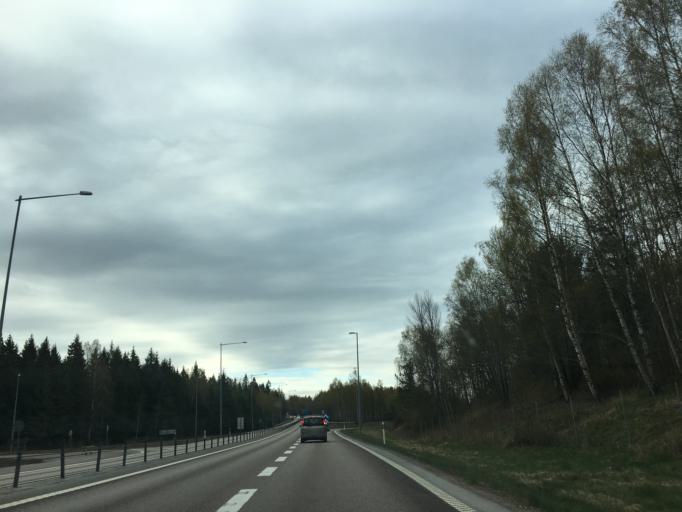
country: SE
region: Vaermland
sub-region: Kristinehamns Kommun
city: Kristinehamn
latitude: 59.3323
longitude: 14.0966
